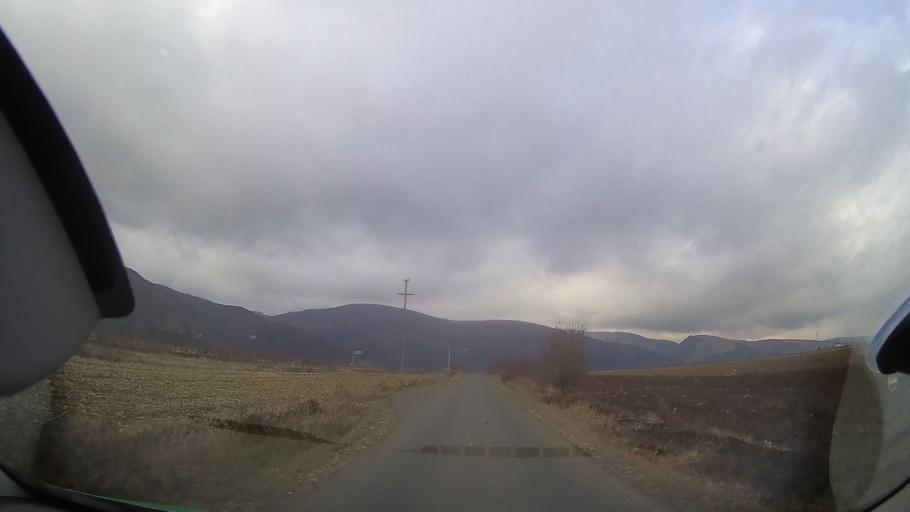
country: RO
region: Cluj
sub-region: Comuna Moldovenesti
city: Moldovenesti
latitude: 46.5057
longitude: 23.6744
